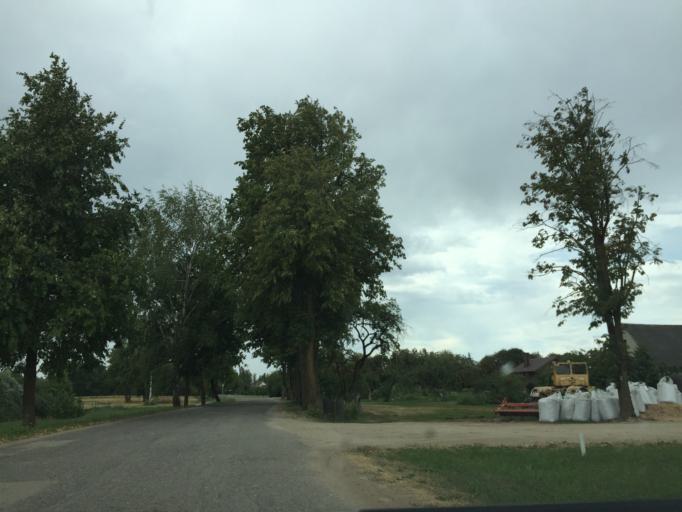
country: LT
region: Siauliu apskritis
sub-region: Joniskis
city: Joniskis
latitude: 56.2722
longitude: 23.7433
